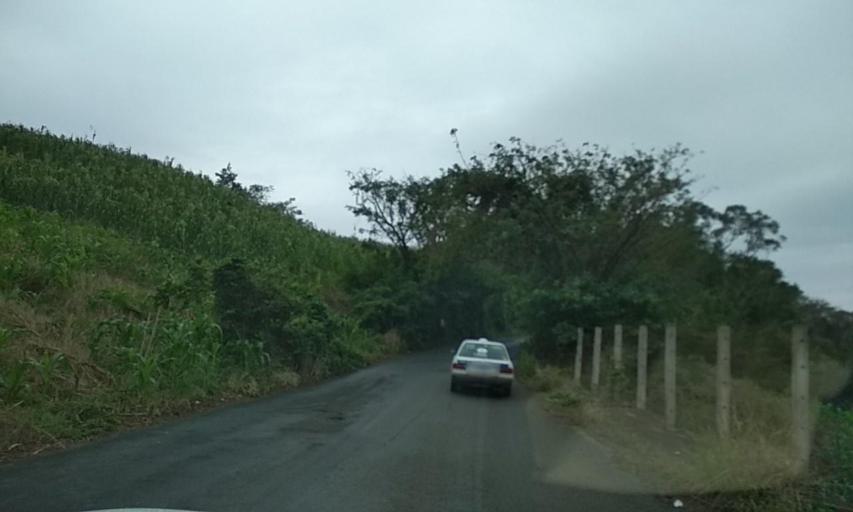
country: MX
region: Veracruz
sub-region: Coatzintla
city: Manuel Maria Contreras
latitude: 20.4449
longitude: -97.4911
